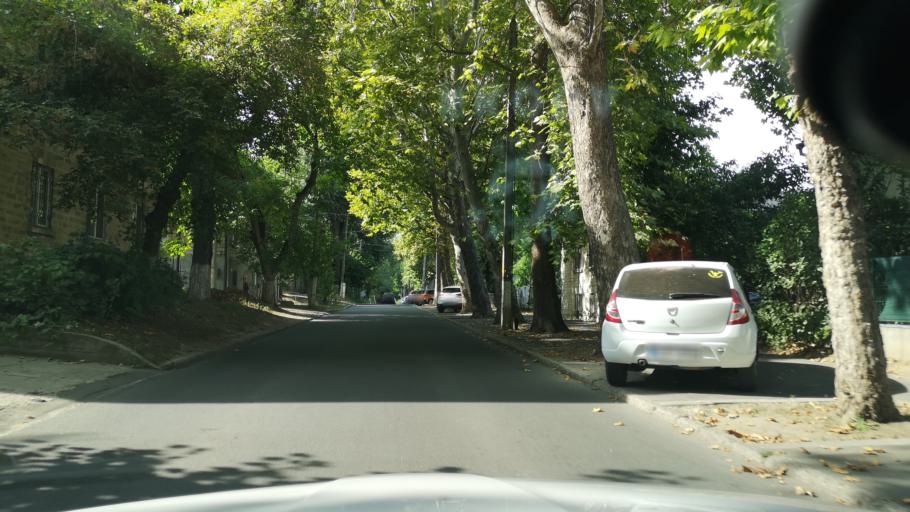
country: MD
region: Chisinau
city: Chisinau
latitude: 47.0340
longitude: 28.8060
